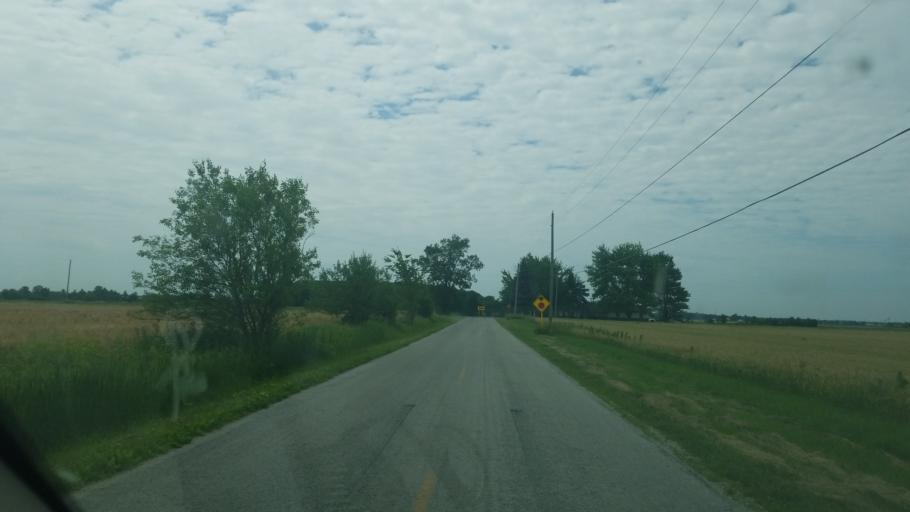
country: US
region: Ohio
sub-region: Wood County
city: North Baltimore
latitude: 41.2235
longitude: -83.6211
